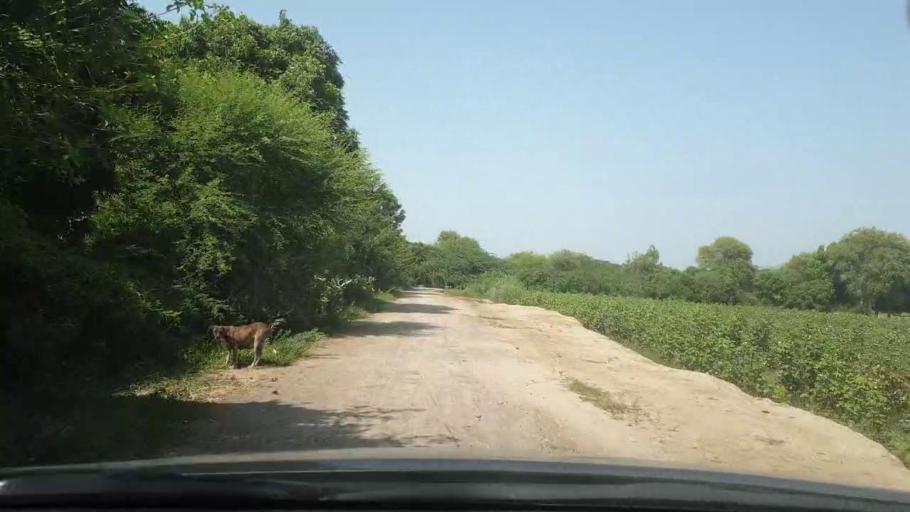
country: PK
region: Sindh
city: Naukot
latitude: 24.8166
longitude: 69.2621
